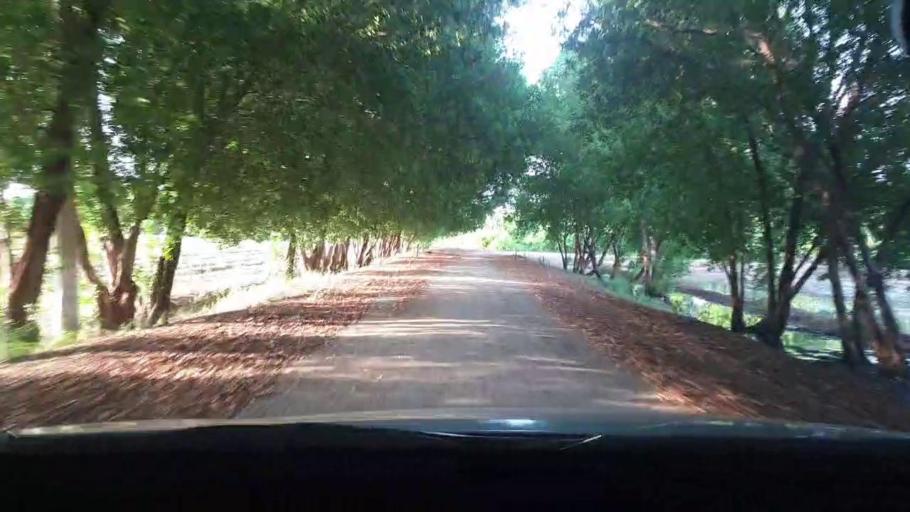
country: PK
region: Sindh
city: Pithoro
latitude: 25.6174
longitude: 69.4423
